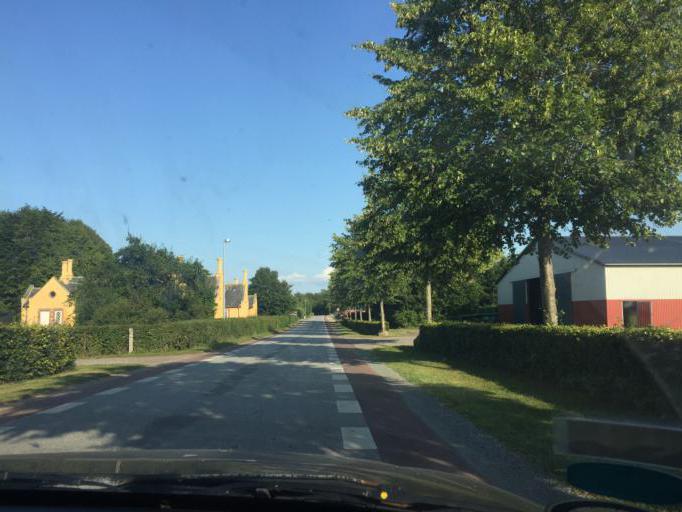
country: DK
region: Zealand
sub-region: Lolland Kommune
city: Maribo
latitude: 54.7992
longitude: 11.5093
